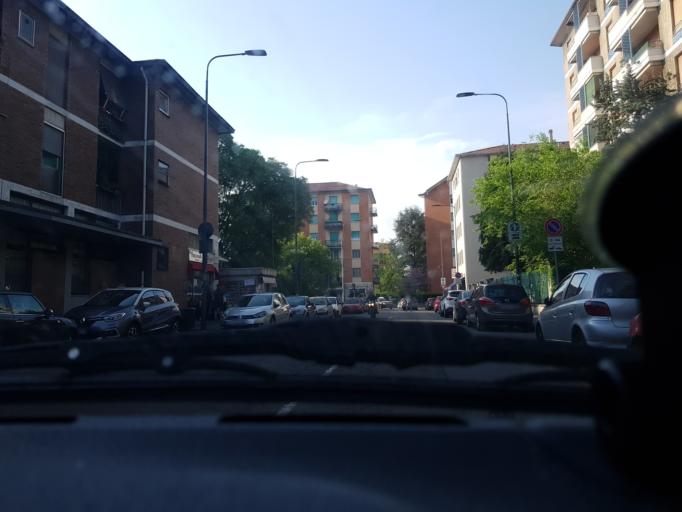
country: IT
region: Lombardy
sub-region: Citta metropolitana di Milano
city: Cesano Boscone
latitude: 45.4574
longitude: 9.0903
